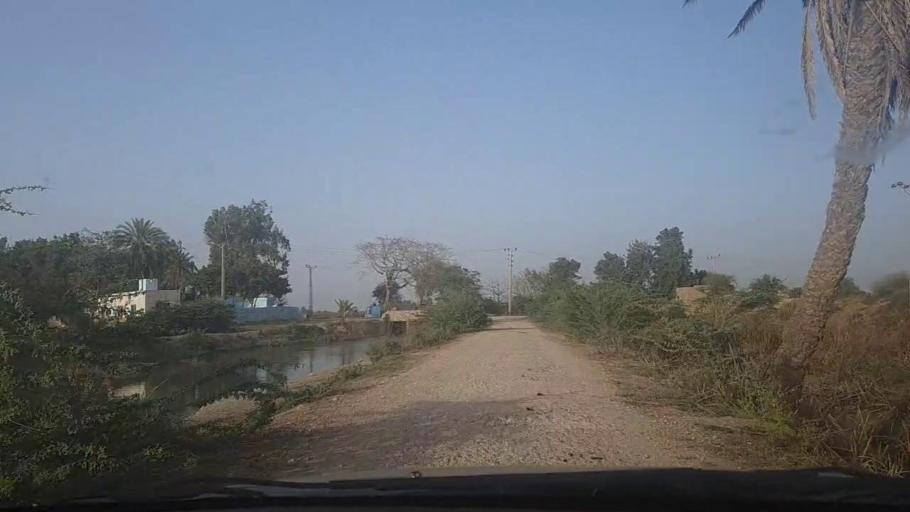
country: PK
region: Sindh
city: Keti Bandar
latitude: 24.2905
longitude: 67.6082
